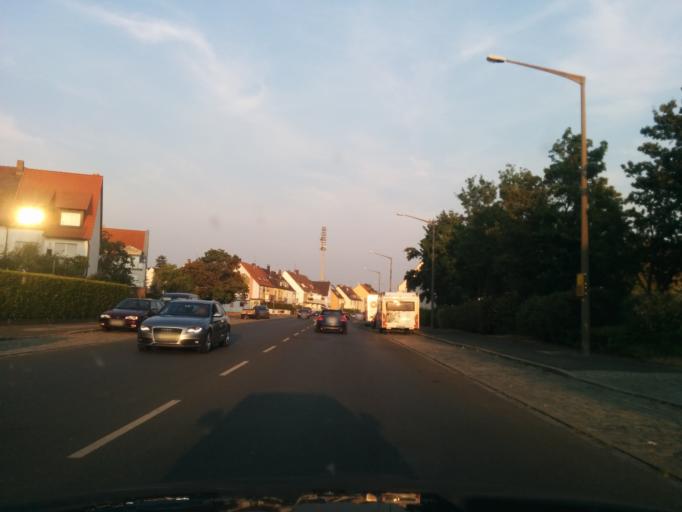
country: DE
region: Bavaria
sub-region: Regierungsbezirk Mittelfranken
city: Wetzendorf
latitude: 49.4691
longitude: 11.0300
